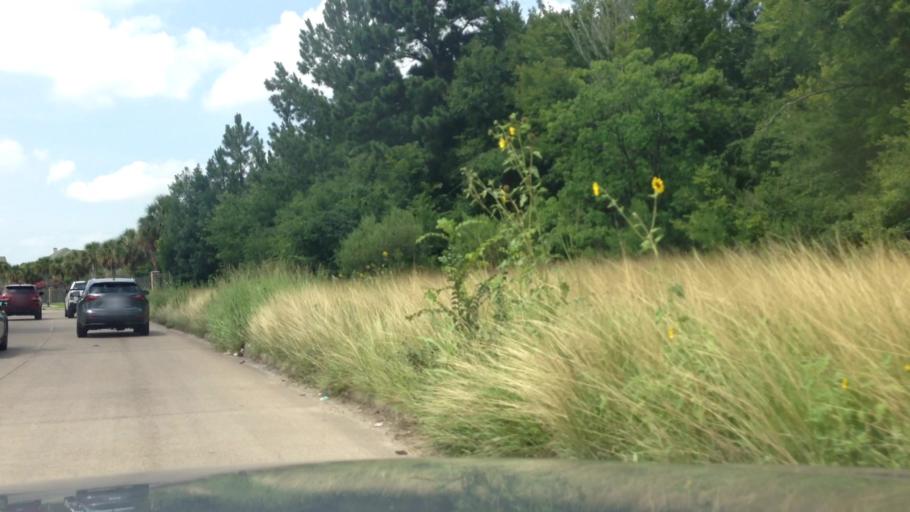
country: US
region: Texas
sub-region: Harris County
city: Jersey Village
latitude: 29.9531
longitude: -95.5471
